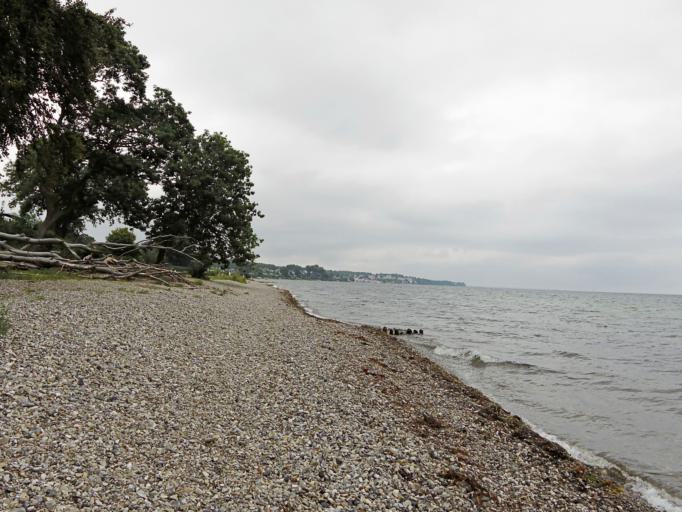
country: DK
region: Capital Region
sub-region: Rudersdal Kommune
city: Trorod
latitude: 55.8061
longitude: 12.5843
